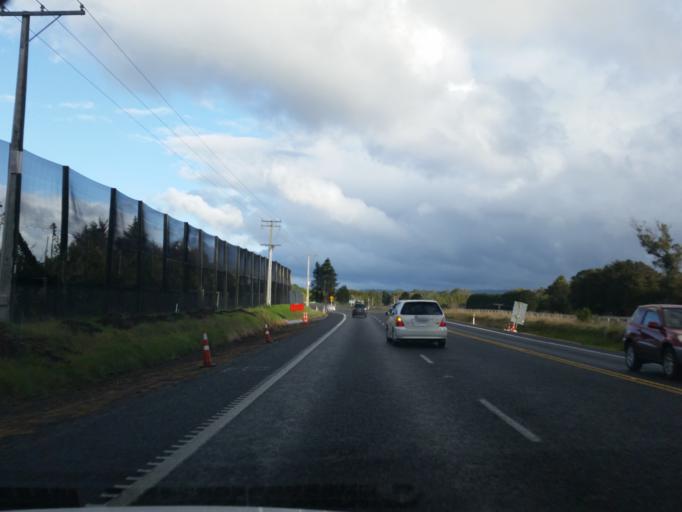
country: NZ
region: Bay of Plenty
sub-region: Western Bay of Plenty District
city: Katikati
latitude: -37.6189
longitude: 175.9510
